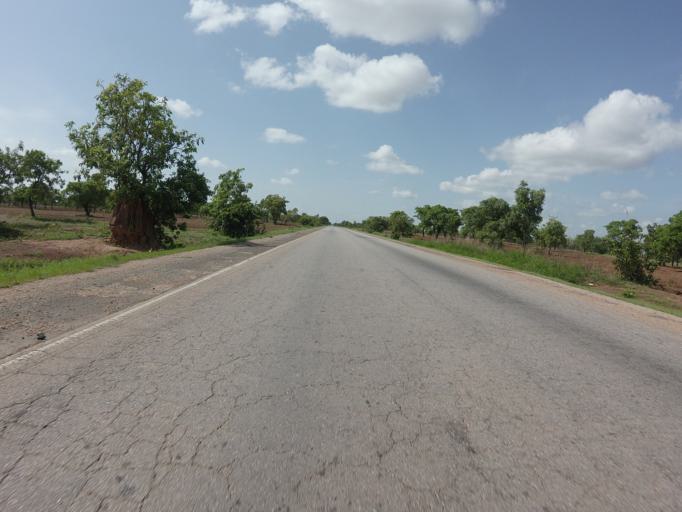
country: GH
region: Northern
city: Savelugu
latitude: 9.9602
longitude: -0.8328
